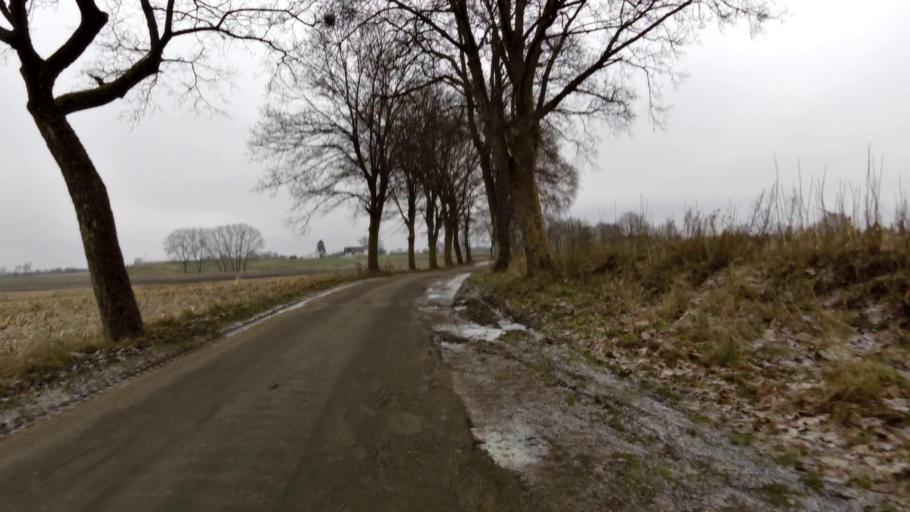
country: PL
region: West Pomeranian Voivodeship
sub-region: Powiat szczecinecki
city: Szczecinek
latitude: 53.6554
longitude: 16.6326
